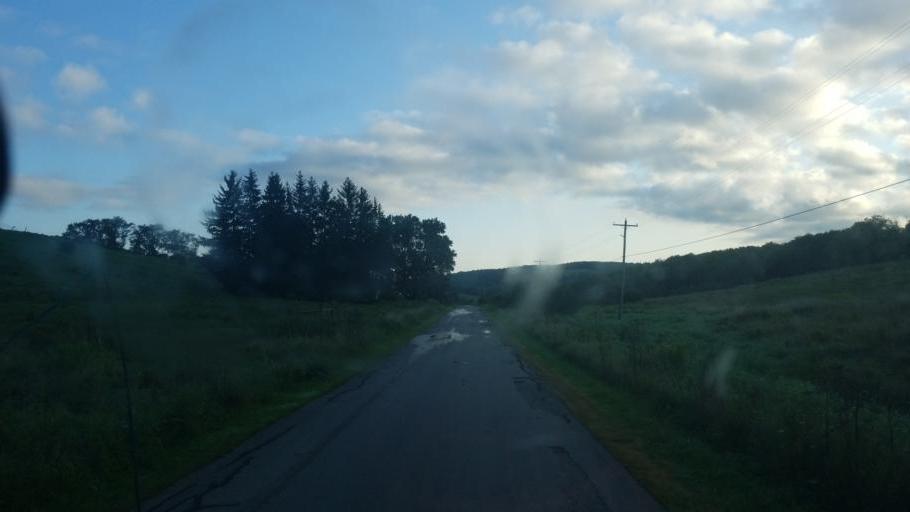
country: US
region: Pennsylvania
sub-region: Potter County
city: Galeton
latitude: 41.8837
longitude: -77.8108
